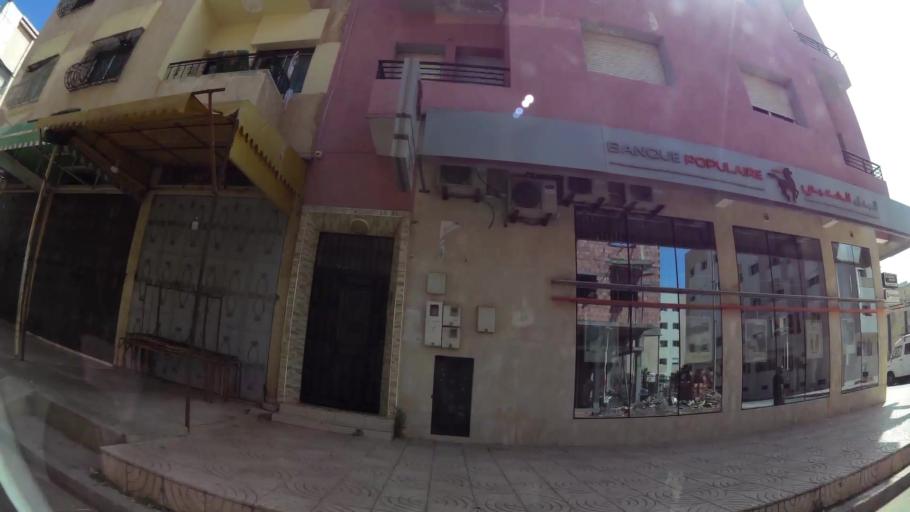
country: MA
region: Rabat-Sale-Zemmour-Zaer
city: Sale
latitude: 34.0748
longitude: -6.7946
